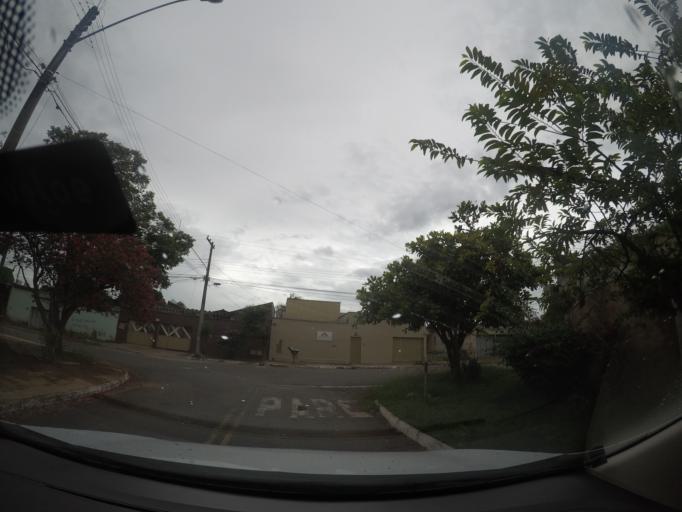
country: BR
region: Goias
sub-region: Goiania
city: Goiania
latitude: -16.7002
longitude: -49.3134
